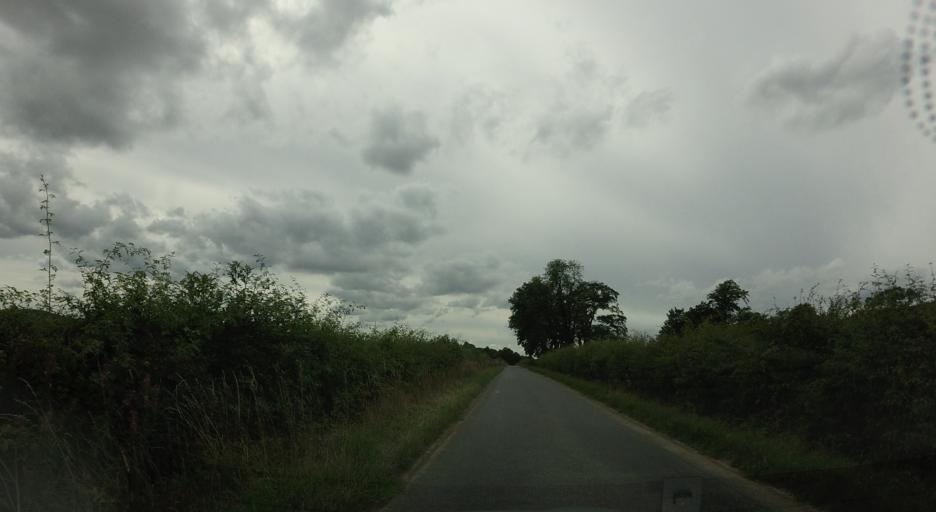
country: GB
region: Scotland
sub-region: Perth and Kinross
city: Bridge of Earn
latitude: 56.3542
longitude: -3.3791
